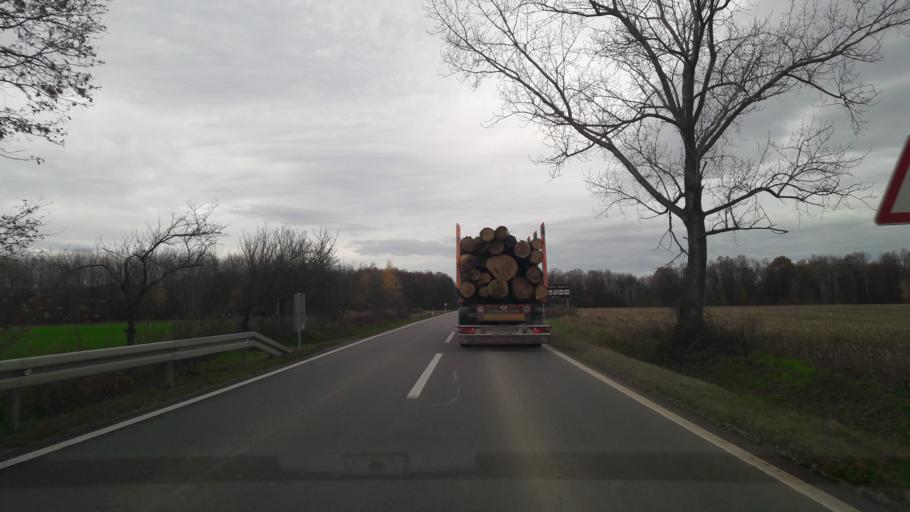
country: HR
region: Virovitick-Podravska
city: Orahovica
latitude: 45.5423
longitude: 17.9187
